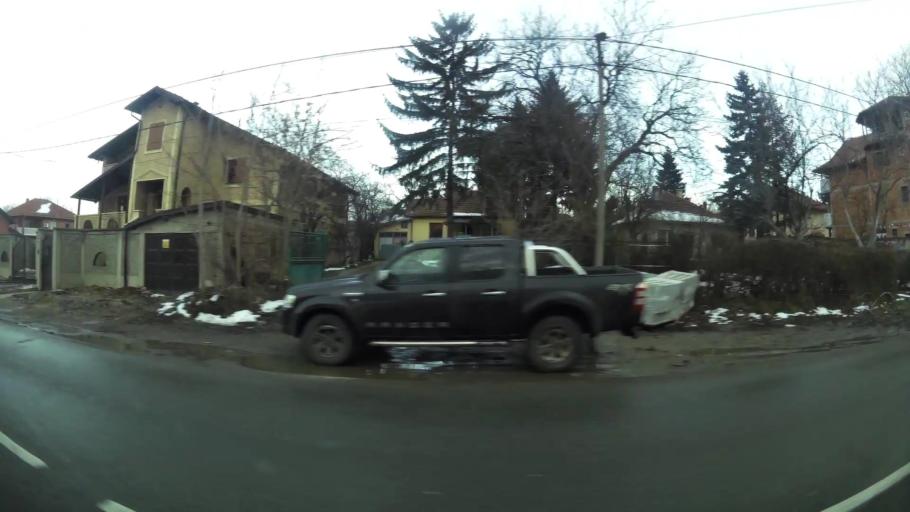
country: RS
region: Central Serbia
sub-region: Belgrade
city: Vozdovac
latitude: 44.7468
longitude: 20.4771
